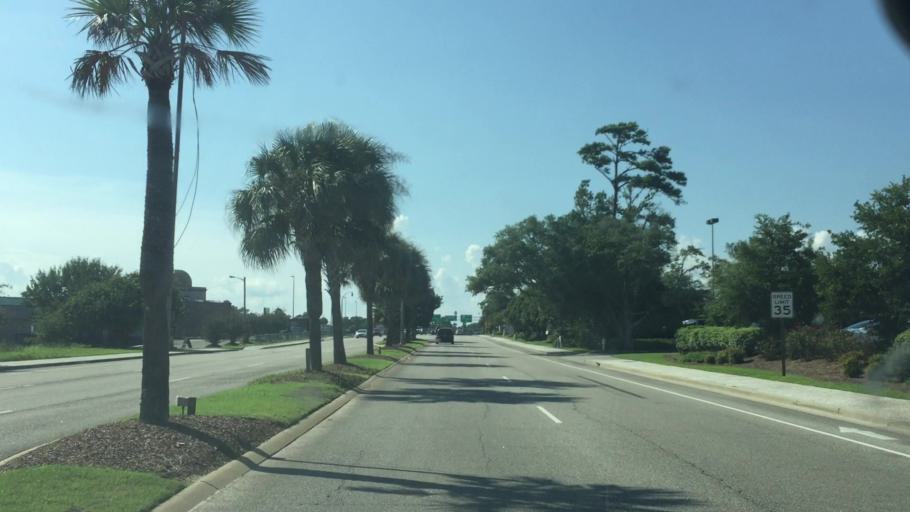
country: US
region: South Carolina
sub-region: Horry County
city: North Myrtle Beach
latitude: 33.8255
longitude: -78.6766
